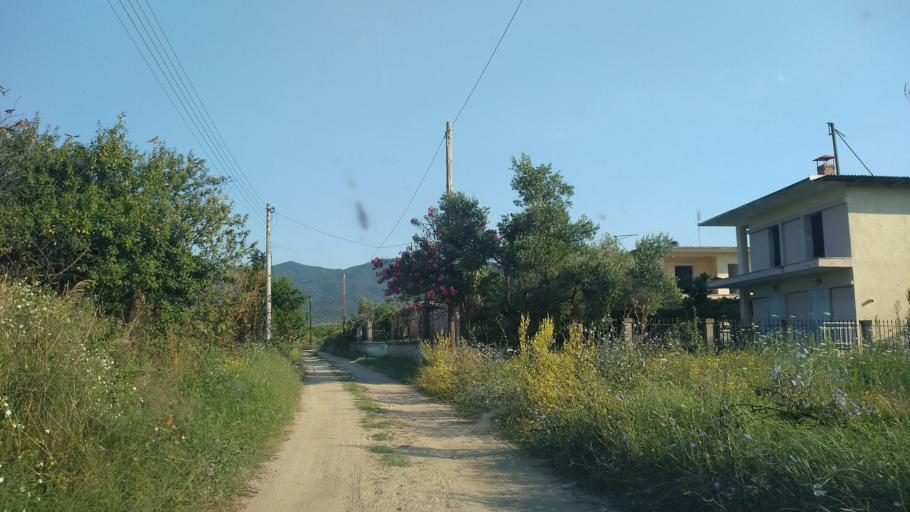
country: GR
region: Central Macedonia
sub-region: Nomos Thessalonikis
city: Nea Vrasna
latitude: 40.6867
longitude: 23.6846
